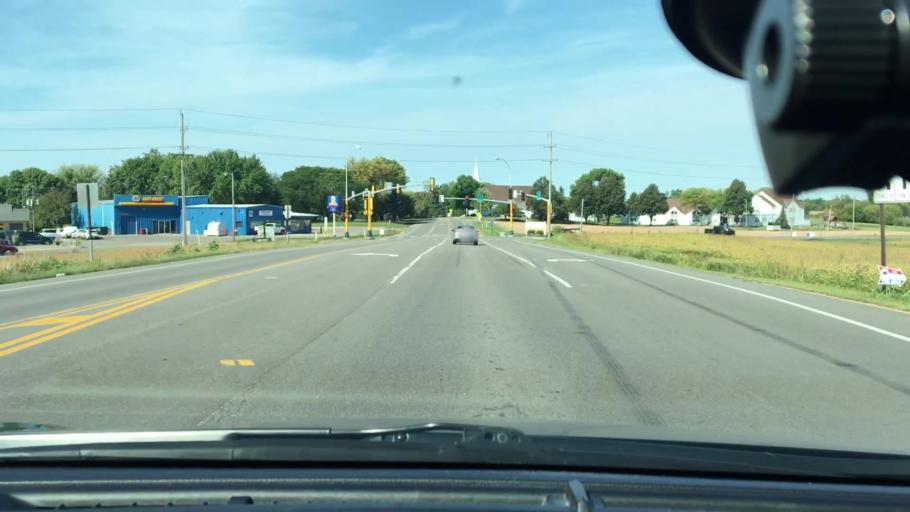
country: US
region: Minnesota
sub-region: Hennepin County
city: Corcoran
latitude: 45.0931
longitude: -93.5418
